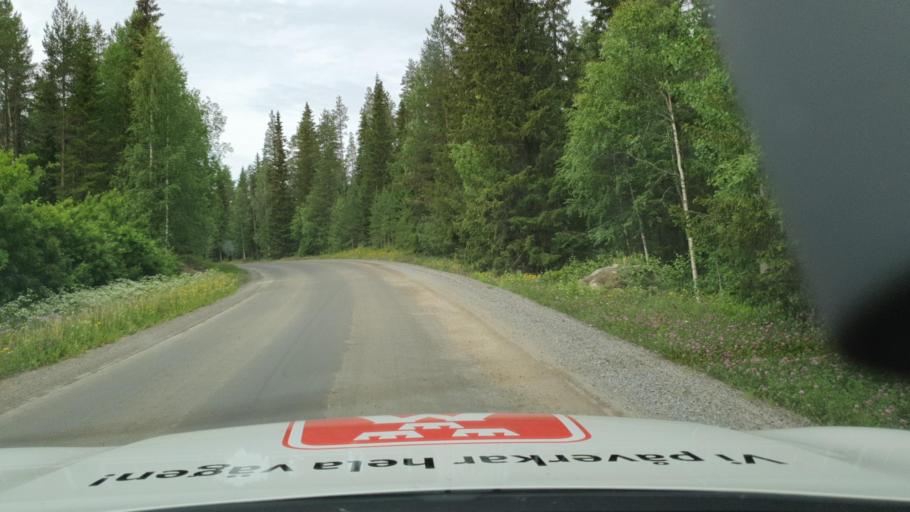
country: SE
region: Vaesterbotten
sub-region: Skelleftea Kommun
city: Burtraesk
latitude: 64.3672
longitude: 20.4007
